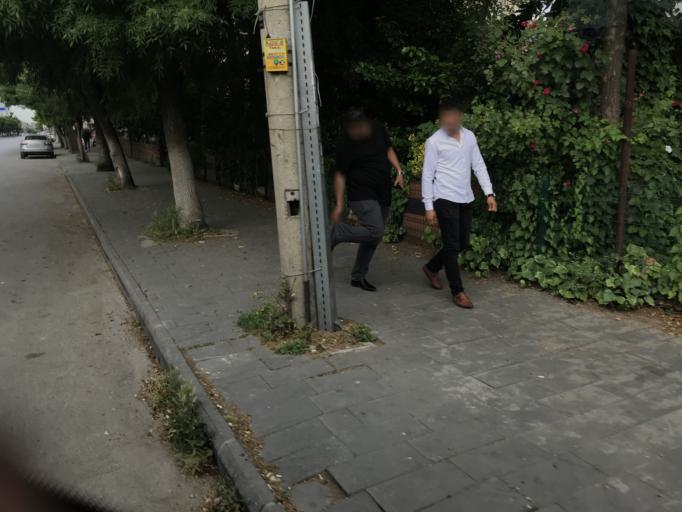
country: TR
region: Gaziantep
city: Sahinbey
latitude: 37.0552
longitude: 37.3391
